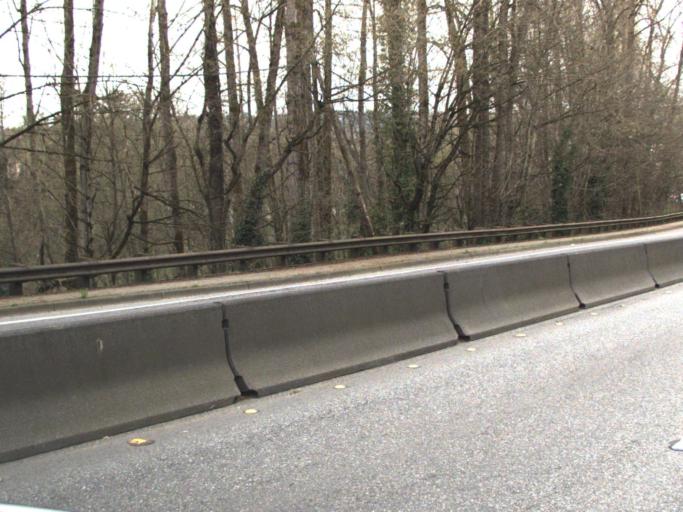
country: US
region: Washington
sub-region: King County
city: Kent
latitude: 47.3824
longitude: -122.2211
